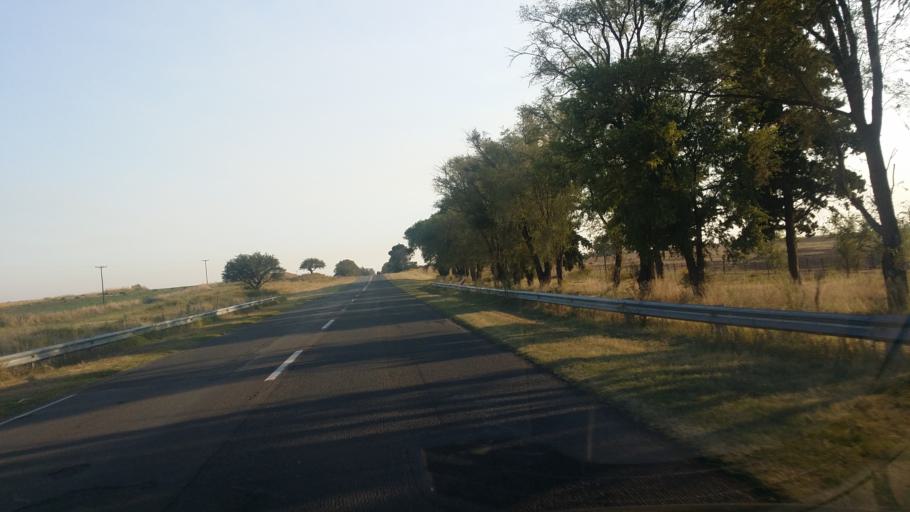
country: AR
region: La Pampa
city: Winifreda
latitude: -36.2093
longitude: -64.2782
